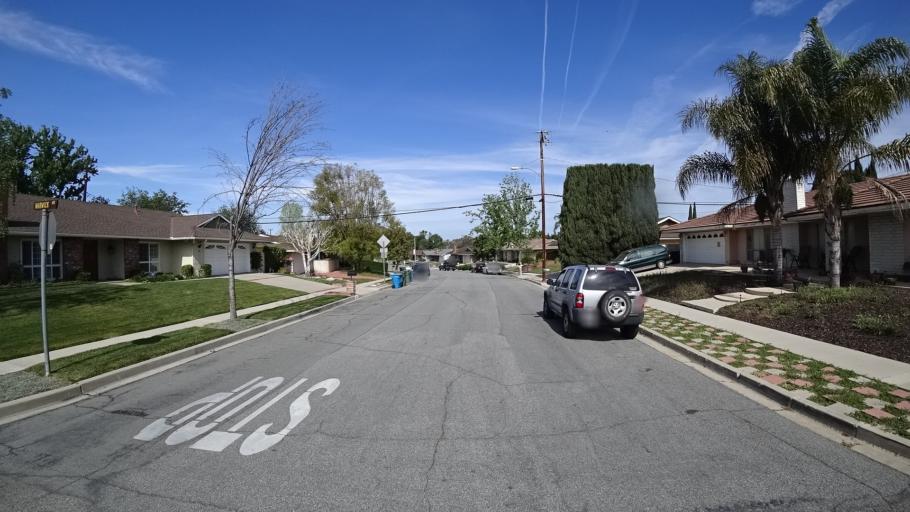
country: US
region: California
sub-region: Ventura County
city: Thousand Oaks
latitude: 34.1935
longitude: -118.8752
